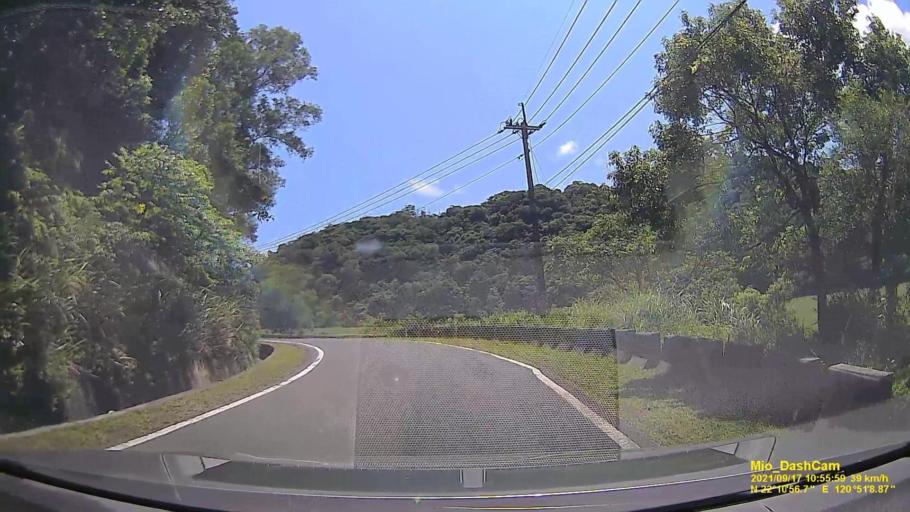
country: TW
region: Taiwan
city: Hengchun
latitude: 22.1824
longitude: 120.8525
